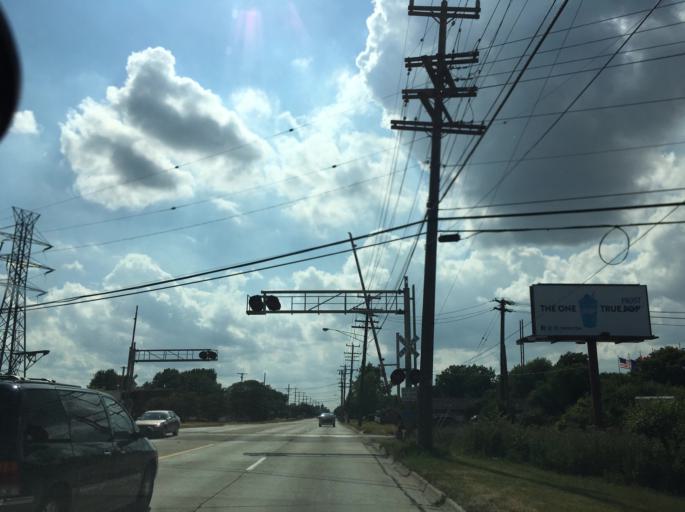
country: US
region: Michigan
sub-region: Macomb County
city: Fraser
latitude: 42.5392
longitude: -82.9374
